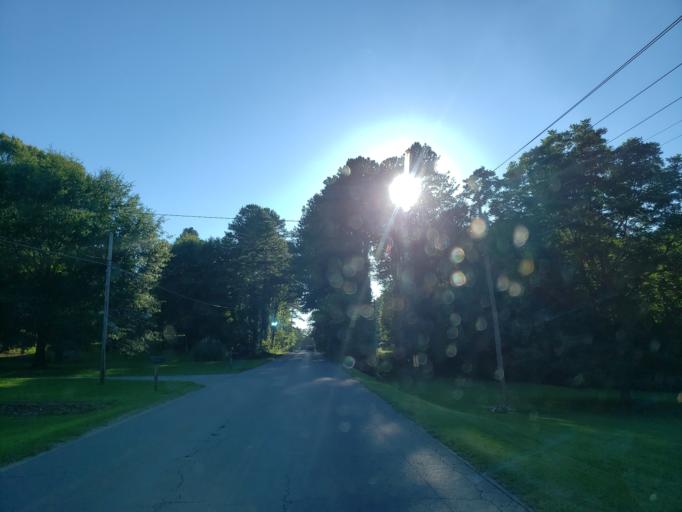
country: US
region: Georgia
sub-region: Polk County
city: Aragon
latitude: 34.0427
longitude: -85.0672
